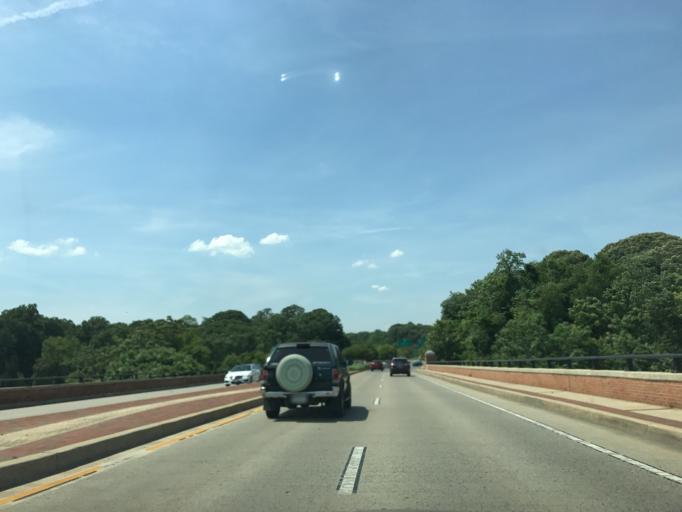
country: US
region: Maryland
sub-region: Anne Arundel County
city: Annapolis
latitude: 38.9913
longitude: -76.5094
